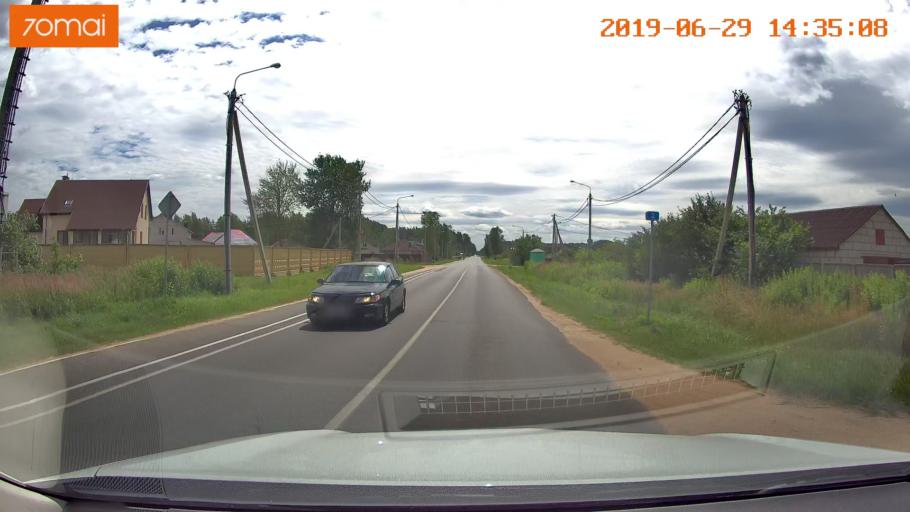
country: BY
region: Minsk
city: Starobin
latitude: 52.7624
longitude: 27.4880
